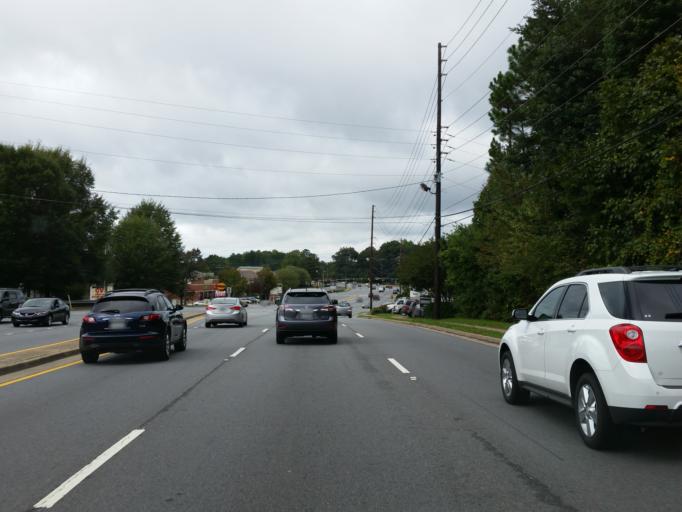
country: US
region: Georgia
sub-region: Fulton County
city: Sandy Springs
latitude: 33.9742
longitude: -84.4137
